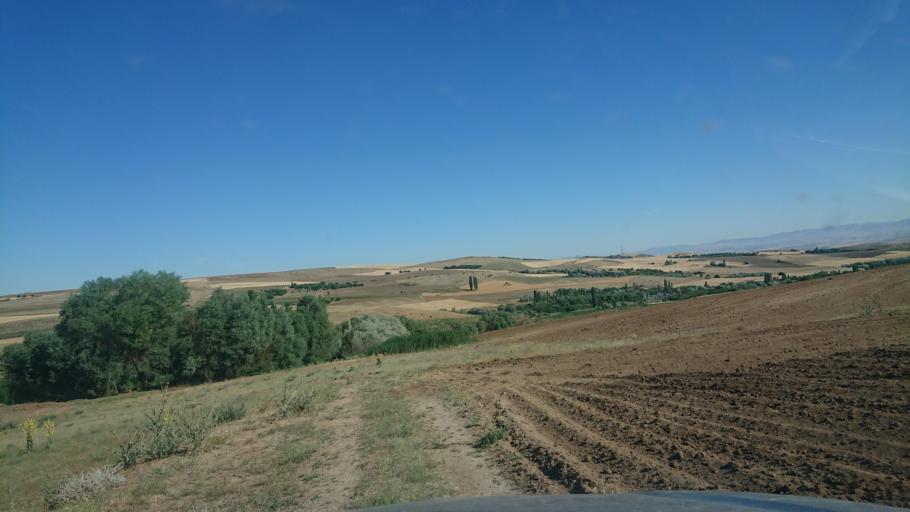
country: TR
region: Aksaray
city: Agacoren
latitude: 38.8411
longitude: 33.9320
